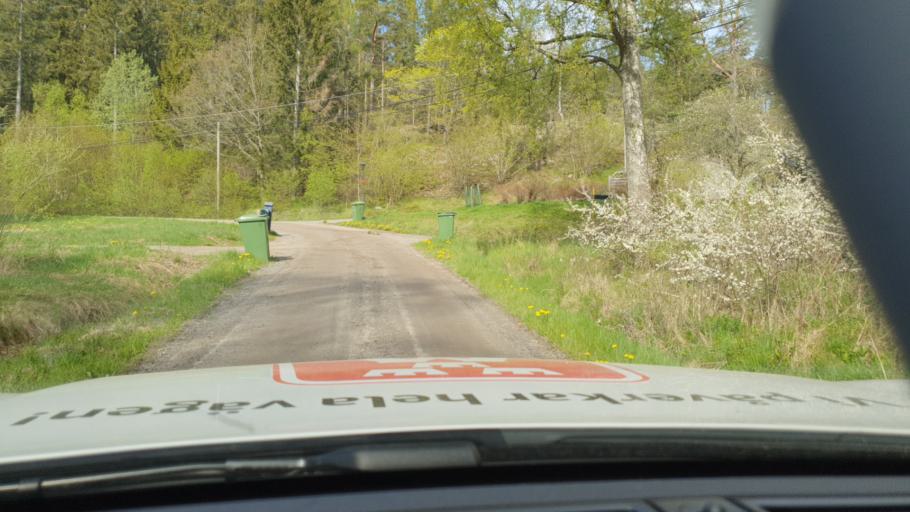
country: SE
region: Stockholm
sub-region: Haninge Kommun
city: Jordbro
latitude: 58.9995
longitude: 18.1419
